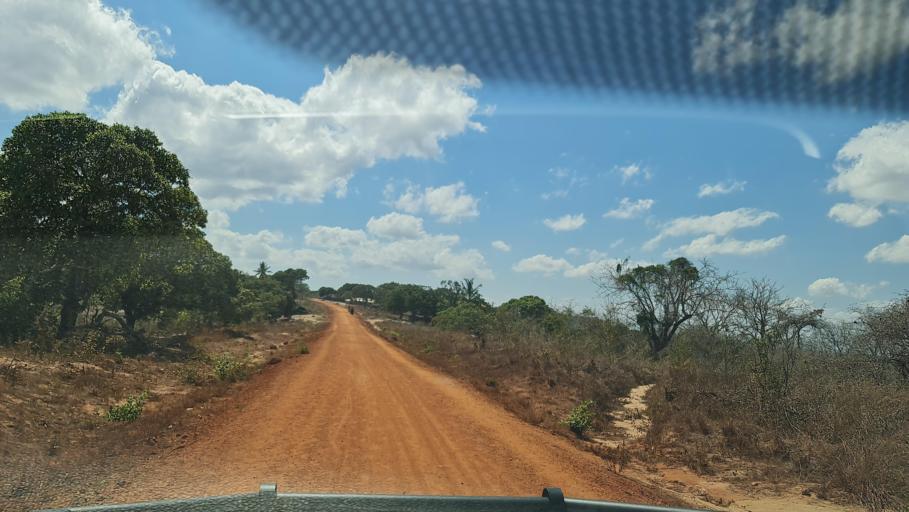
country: MZ
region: Nampula
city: Nacala
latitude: -14.1757
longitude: 40.2078
